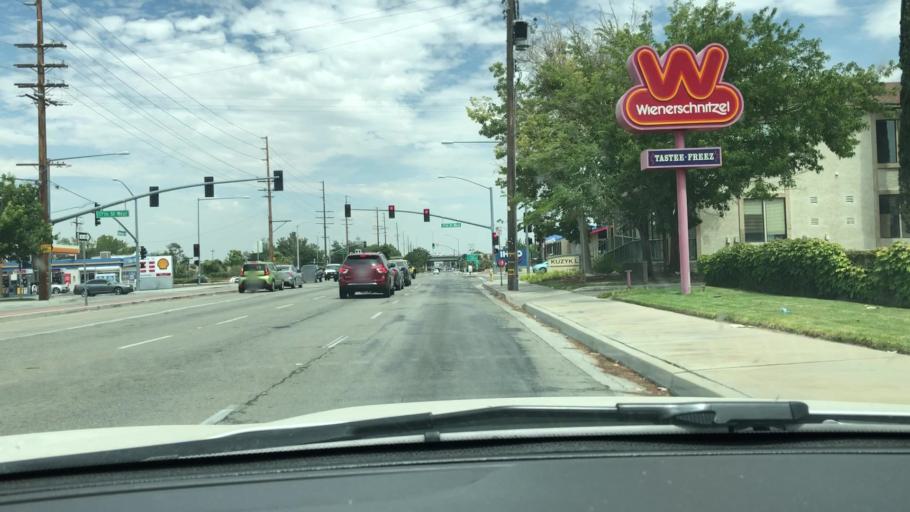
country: US
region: California
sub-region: Los Angeles County
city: Lancaster
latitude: 34.6749
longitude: -118.1621
